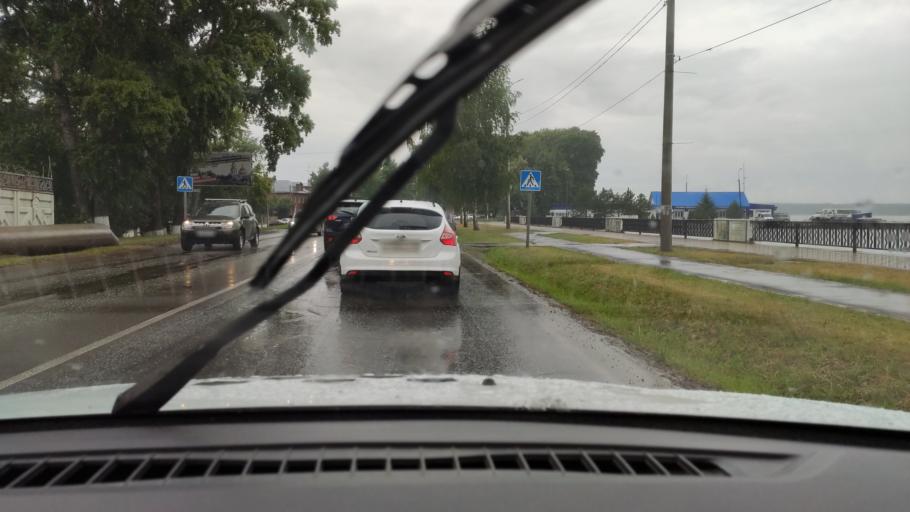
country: RU
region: Udmurtiya
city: Votkinsk
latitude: 57.0516
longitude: 53.9744
